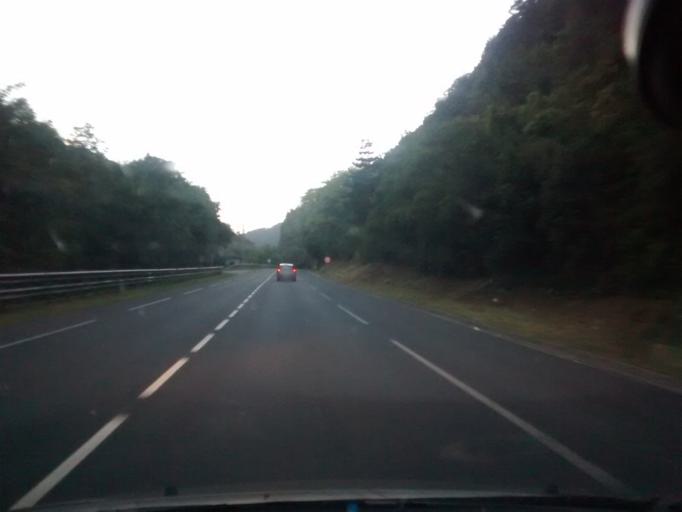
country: ES
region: Basque Country
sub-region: Provincia de Guipuzcoa
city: Mendaro
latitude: 43.2638
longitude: -2.3767
